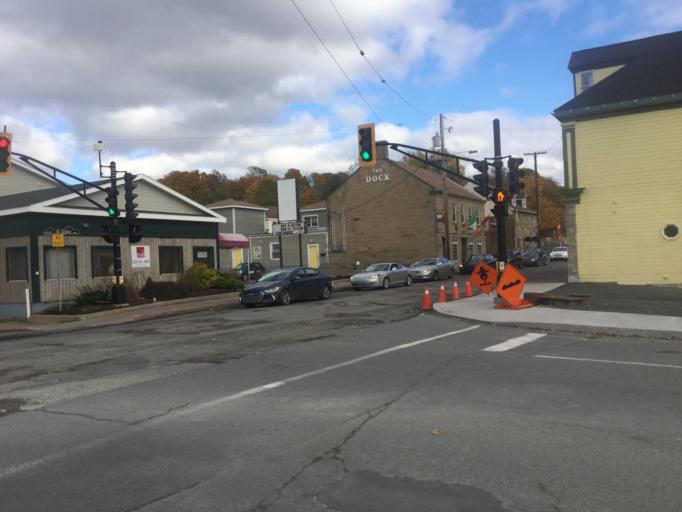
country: CA
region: Nova Scotia
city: New Glasgow
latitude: 45.5894
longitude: -62.6457
